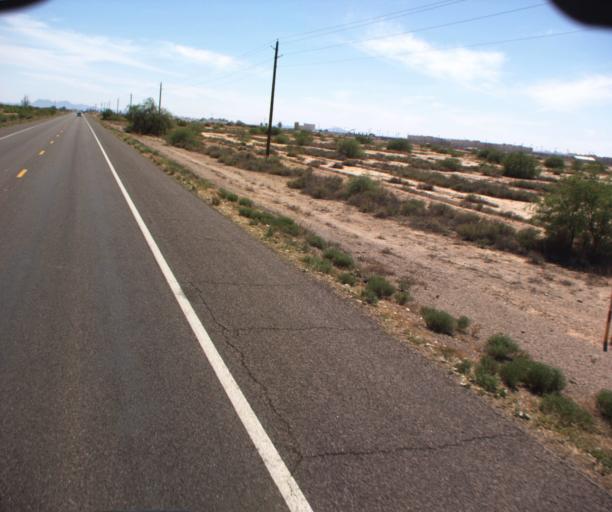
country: US
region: Arizona
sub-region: Pinal County
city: Eloy
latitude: 32.8140
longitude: -111.5154
